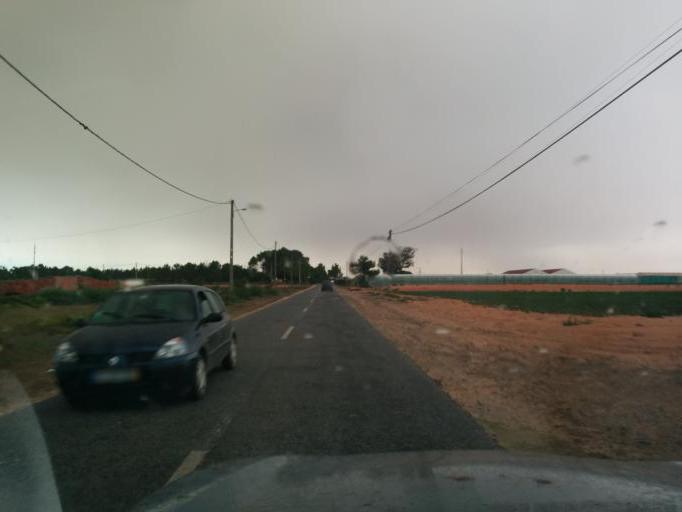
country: PT
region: Beja
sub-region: Odemira
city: Vila Nova de Milfontes
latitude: 37.6048
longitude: -8.8003
